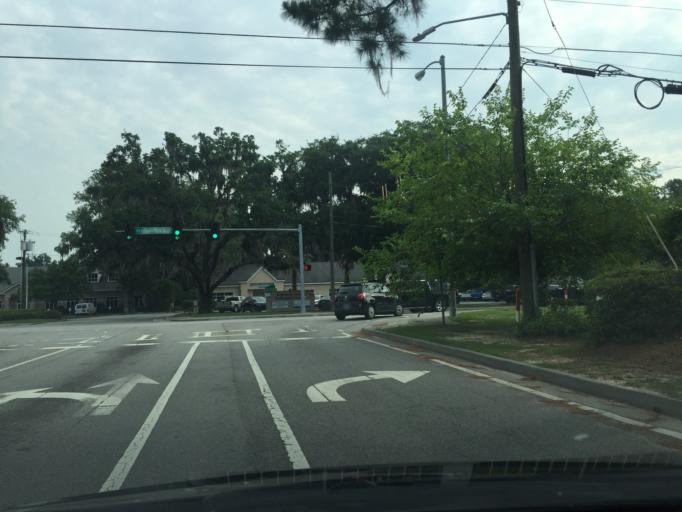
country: US
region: Georgia
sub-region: Chatham County
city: Isle of Hope
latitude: 32.0121
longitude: -81.1081
